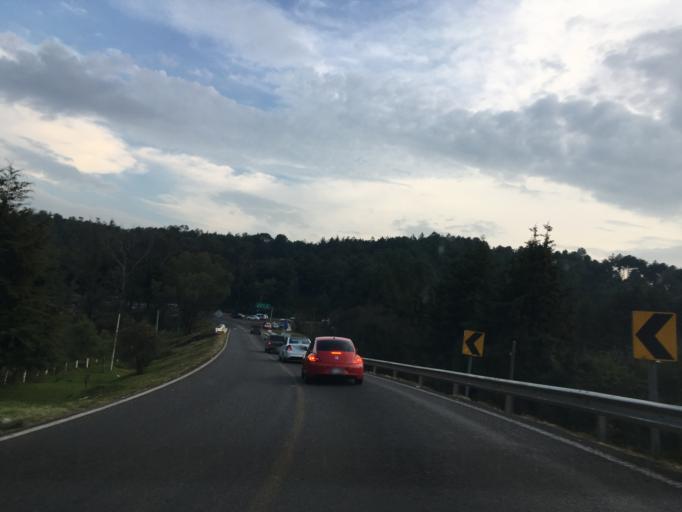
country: MX
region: Michoacan
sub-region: Patzcuaro
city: Santa Maria Huiramangaro (San Juan Tumbio)
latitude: 19.4846
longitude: -101.7406
